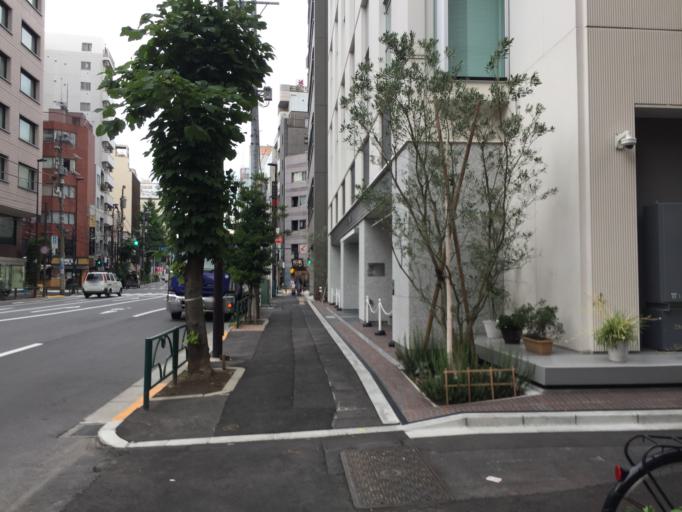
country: JP
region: Tokyo
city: Tokyo
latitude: 35.7068
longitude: 139.7701
